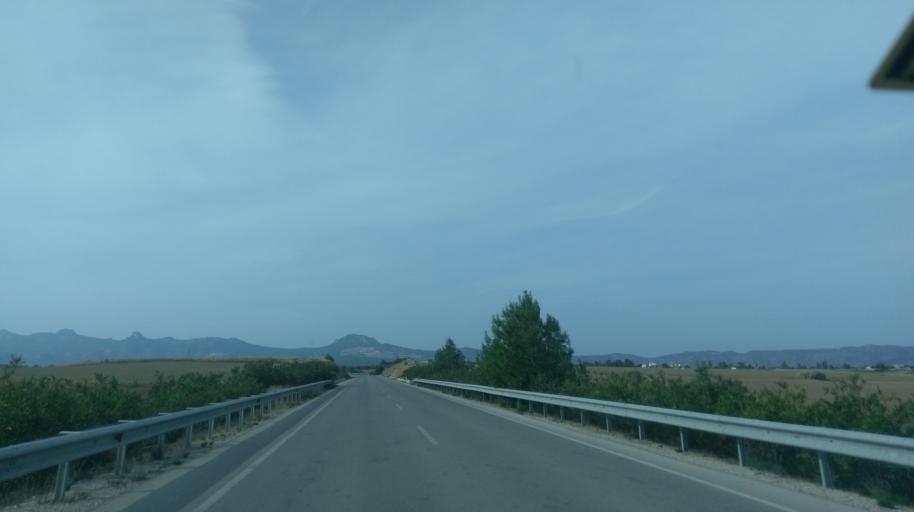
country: CY
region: Ammochostos
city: Leonarisso
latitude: 35.3810
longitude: 34.0203
